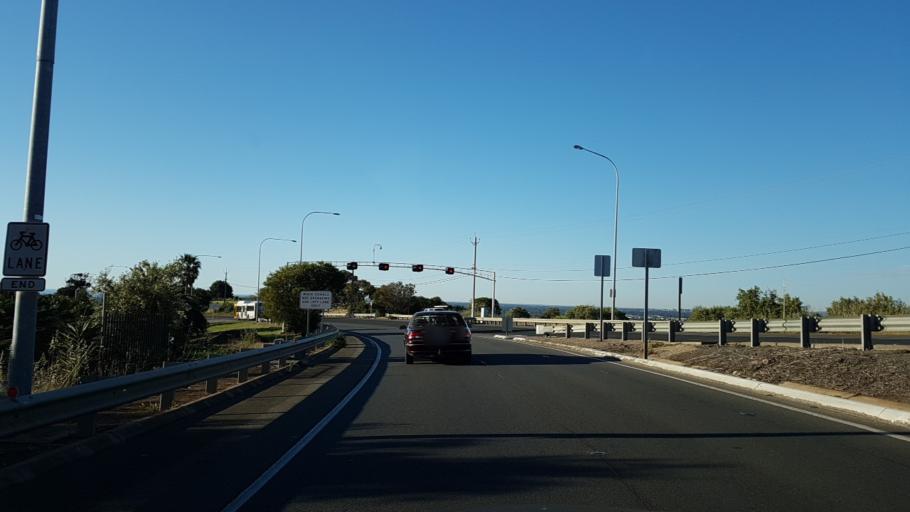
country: AU
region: South Australia
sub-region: Onkaparinga
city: Bedford Park
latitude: -35.0340
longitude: 138.5634
